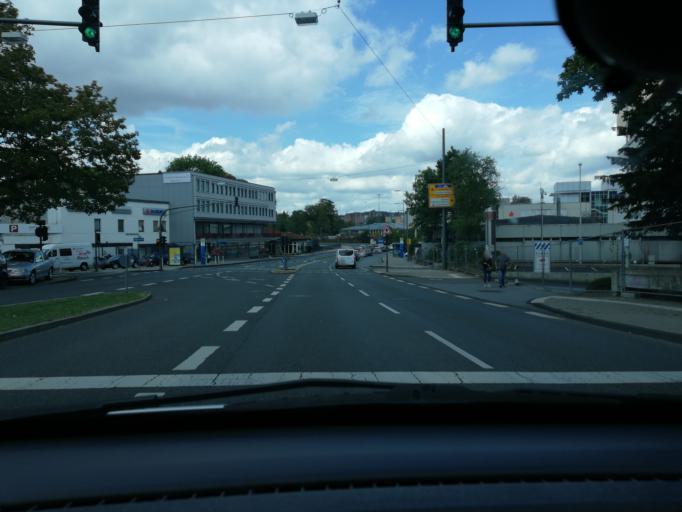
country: DE
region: North Rhine-Westphalia
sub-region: Regierungsbezirk Dusseldorf
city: Wuppertal
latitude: 51.2522
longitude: 7.1466
